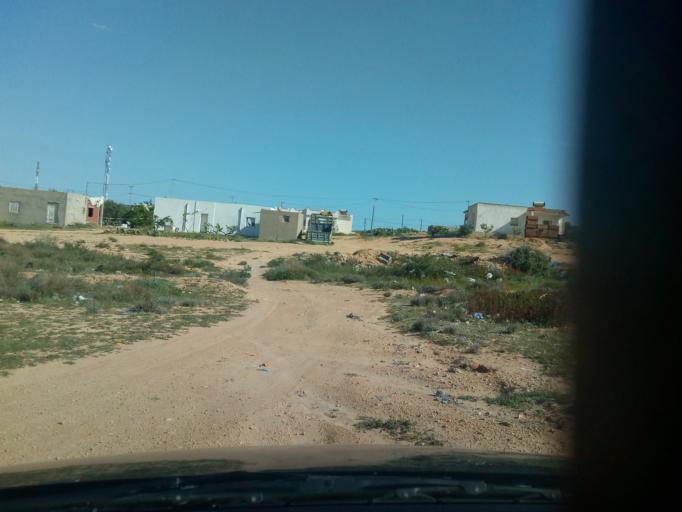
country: TN
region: Safaqis
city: Sfax
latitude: 34.7291
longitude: 10.6028
